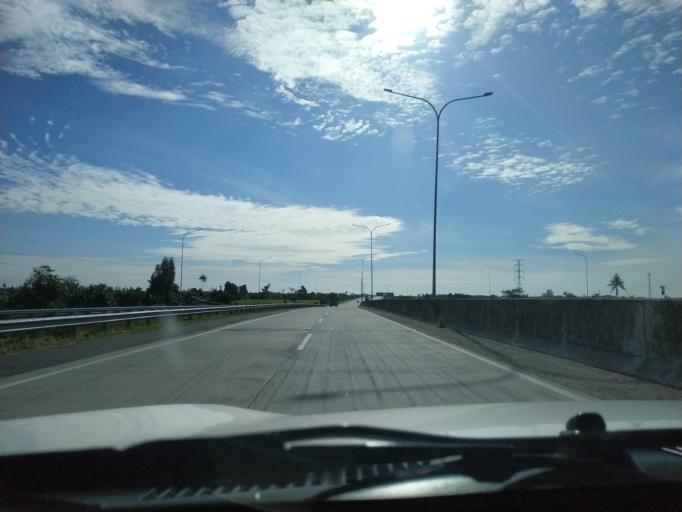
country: ID
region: North Sumatra
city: Percut
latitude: 3.5365
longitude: 98.8563
